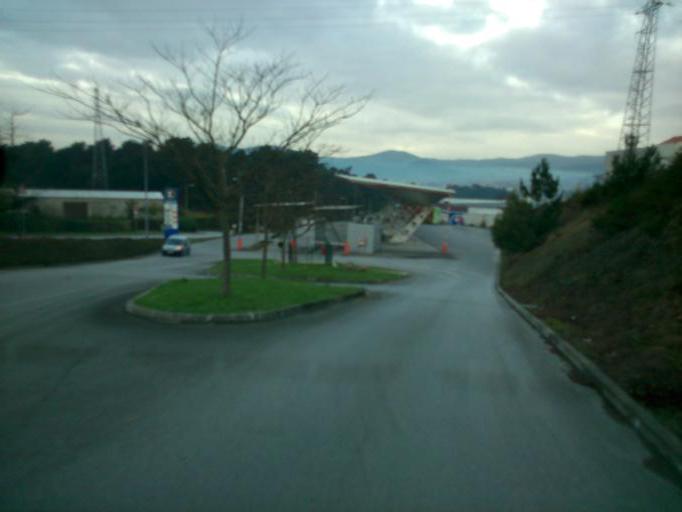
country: PT
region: Braga
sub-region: Barcelos
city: Barcelos
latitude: 41.5209
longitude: -8.6081
